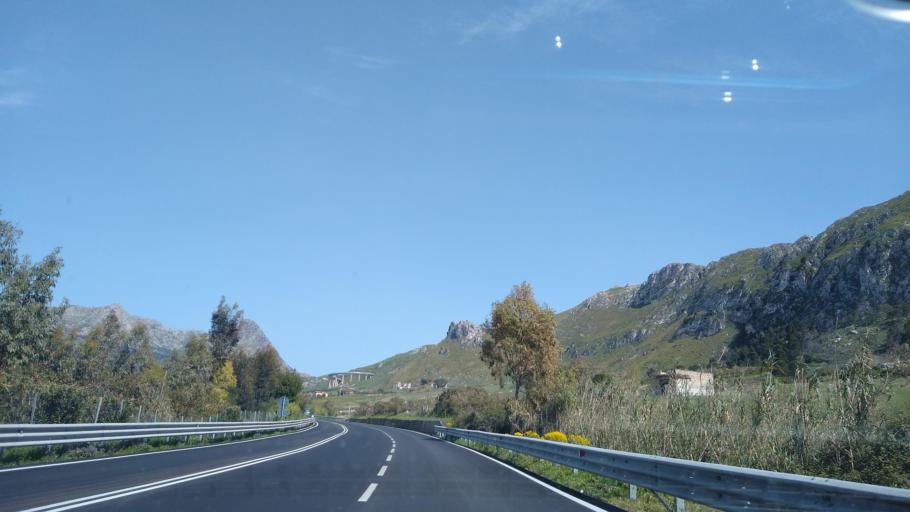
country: IT
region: Sicily
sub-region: Palermo
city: San Giuseppe Jato
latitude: 37.9747
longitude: 13.2078
